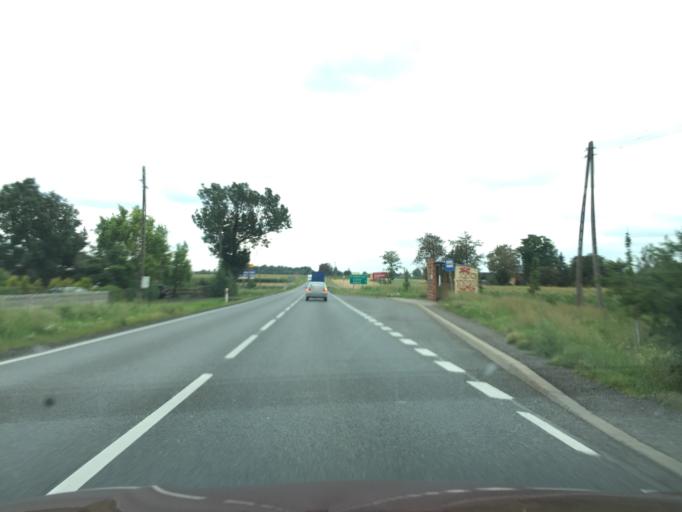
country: PL
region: Greater Poland Voivodeship
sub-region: Kalisz
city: Kalisz
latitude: 51.8251
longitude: 18.0941
